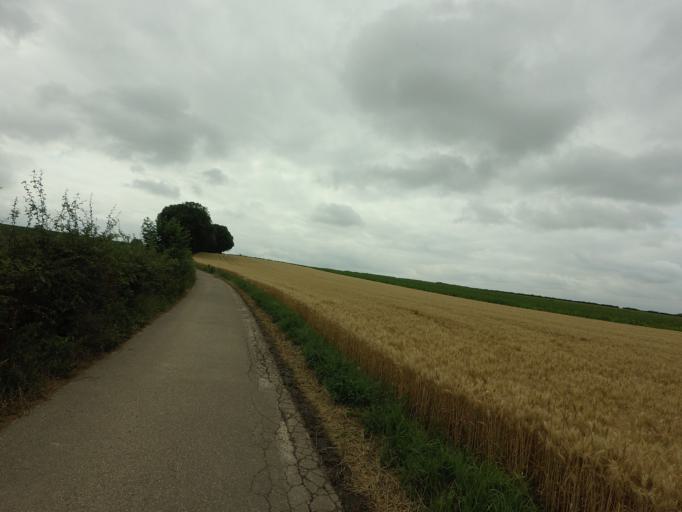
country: NL
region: Limburg
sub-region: Eijsden-Margraten
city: Margraten
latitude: 50.8148
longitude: 5.8181
